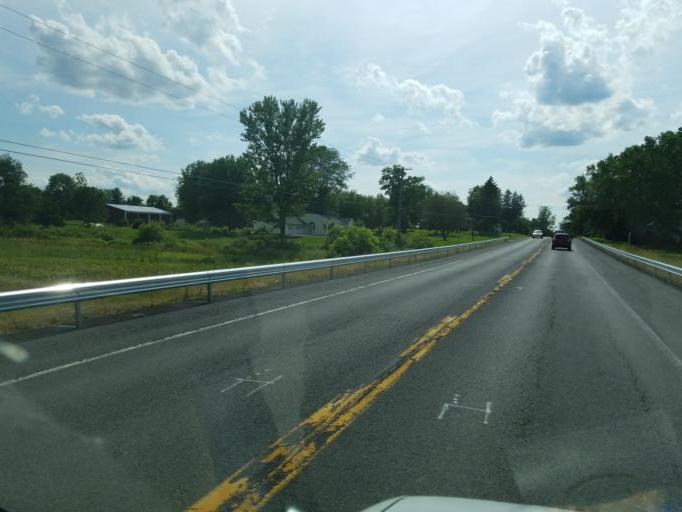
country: US
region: New York
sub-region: Ontario County
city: Clifton Springs
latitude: 42.8609
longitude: -77.1419
